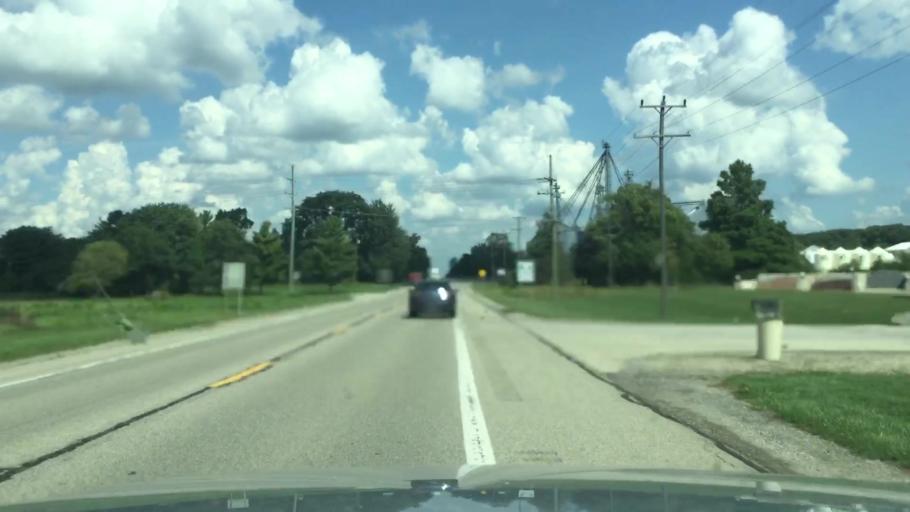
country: US
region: Michigan
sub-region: Washtenaw County
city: Saline
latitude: 42.1478
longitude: -83.8268
